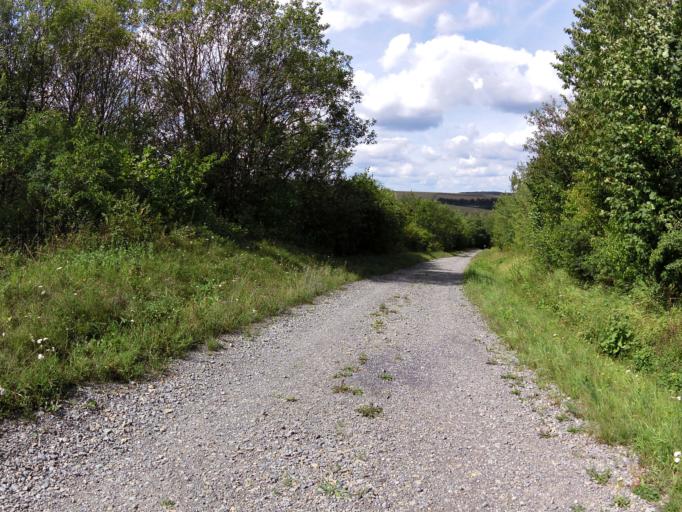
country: DE
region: Bavaria
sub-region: Regierungsbezirk Unterfranken
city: Margetshochheim
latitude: 49.8358
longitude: 9.8428
